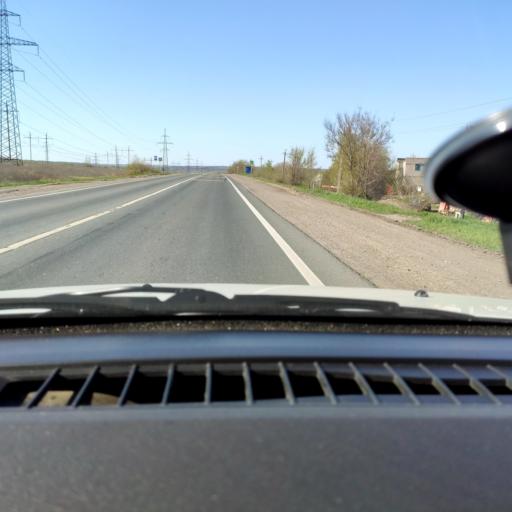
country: RU
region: Samara
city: Dubovyy Umet
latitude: 53.0719
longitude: 50.3831
